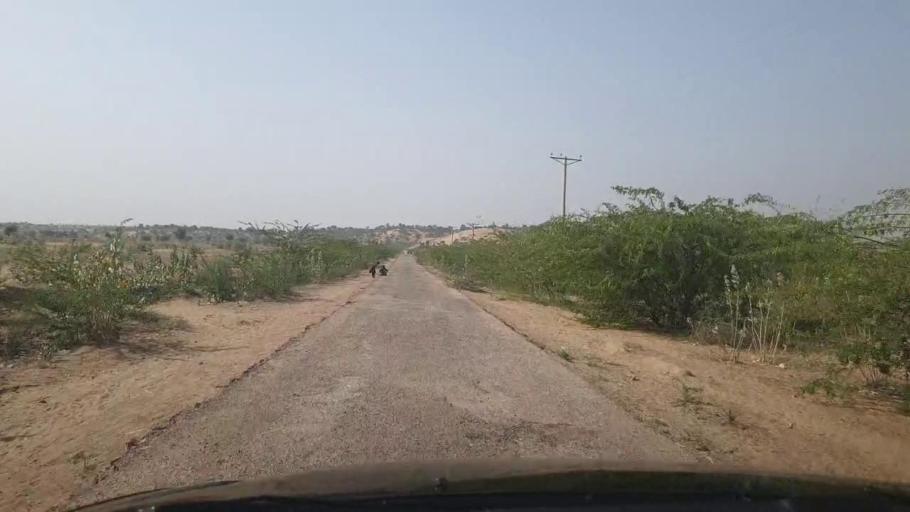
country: PK
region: Sindh
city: Islamkot
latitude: 25.0066
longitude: 70.2112
